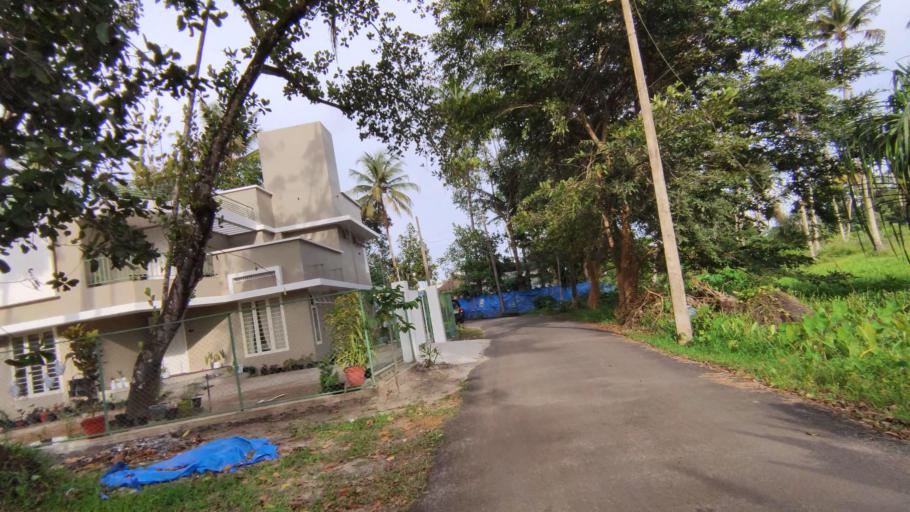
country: IN
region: Kerala
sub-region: Alappuzha
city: Shertallai
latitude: 9.6245
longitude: 76.3336
